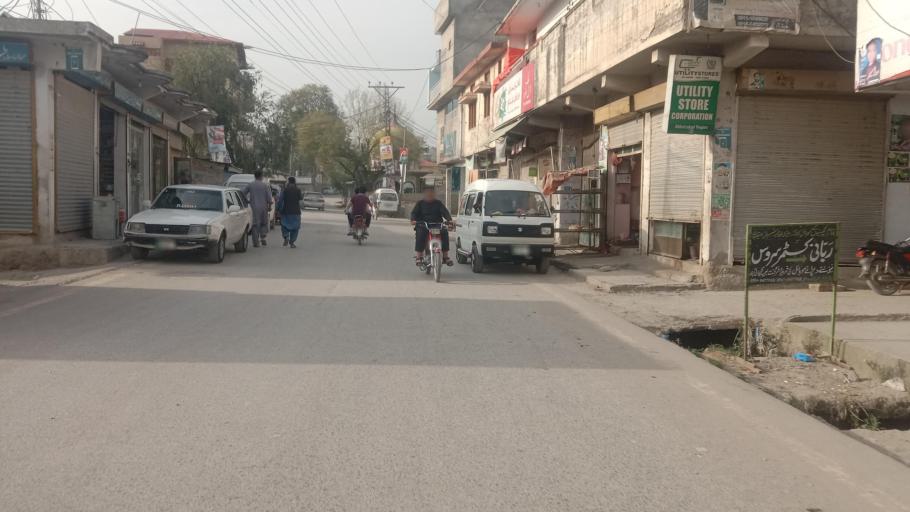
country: PK
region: Khyber Pakhtunkhwa
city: Abbottabad
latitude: 34.1588
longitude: 73.2643
